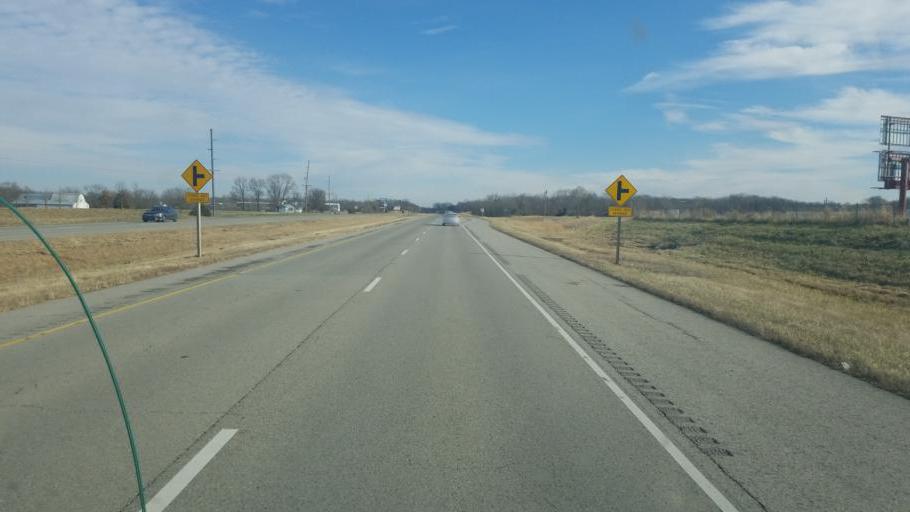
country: US
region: Illinois
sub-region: Williamson County
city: Marion
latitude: 37.7295
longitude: -88.8393
